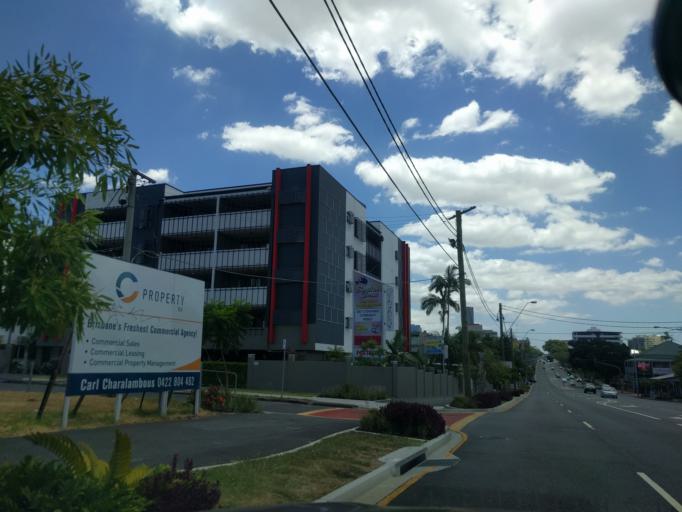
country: AU
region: Queensland
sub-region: Brisbane
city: Woolloongabba
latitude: -27.4823
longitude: 153.0358
